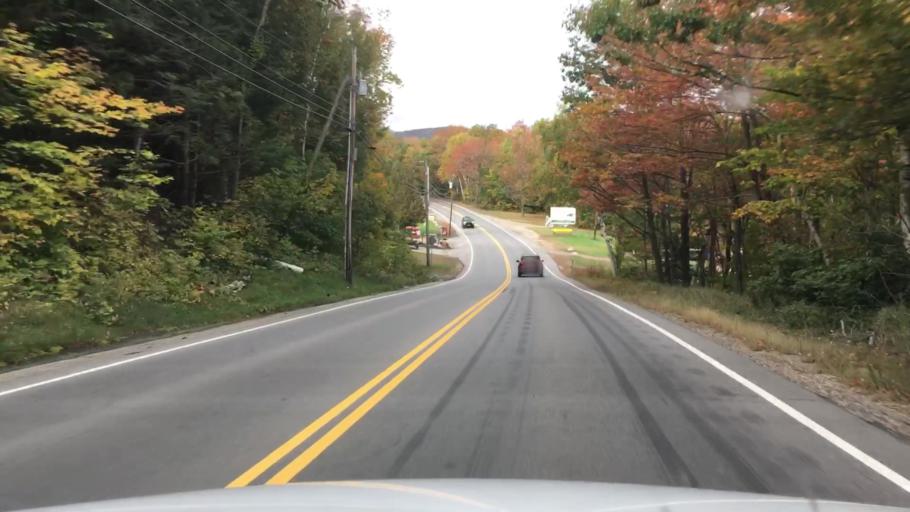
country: US
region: New Hampshire
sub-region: Coos County
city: Gorham
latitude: 44.3874
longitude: -71.1383
